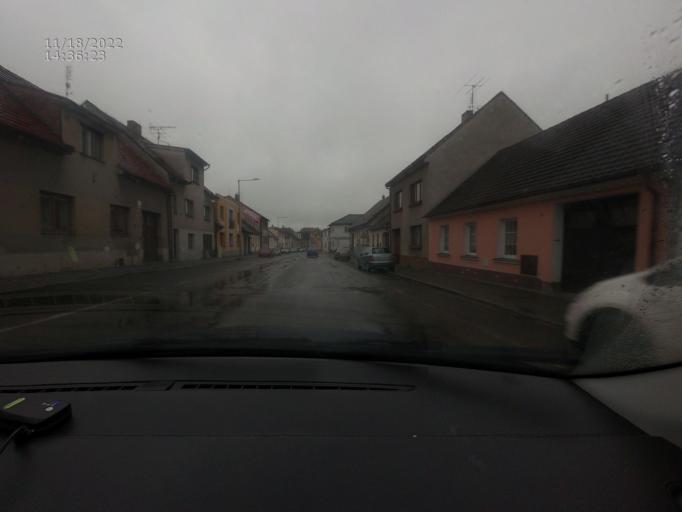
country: CZ
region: Jihocesky
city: Milevsko
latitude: 49.4512
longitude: 14.3546
